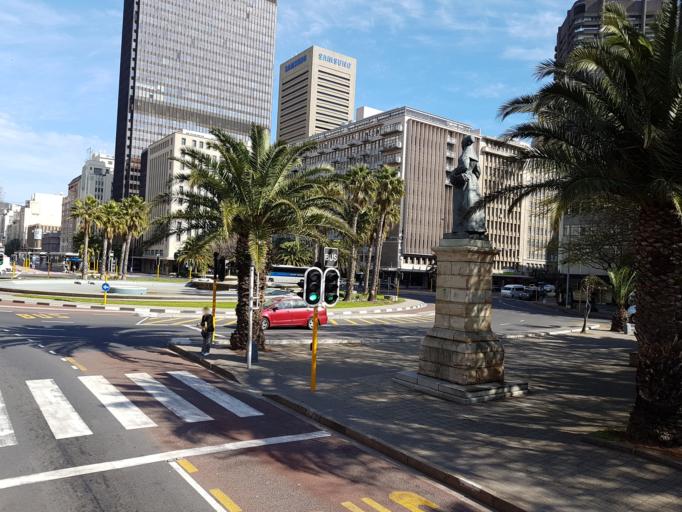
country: ZA
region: Western Cape
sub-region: City of Cape Town
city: Cape Town
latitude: -33.9195
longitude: 18.4262
